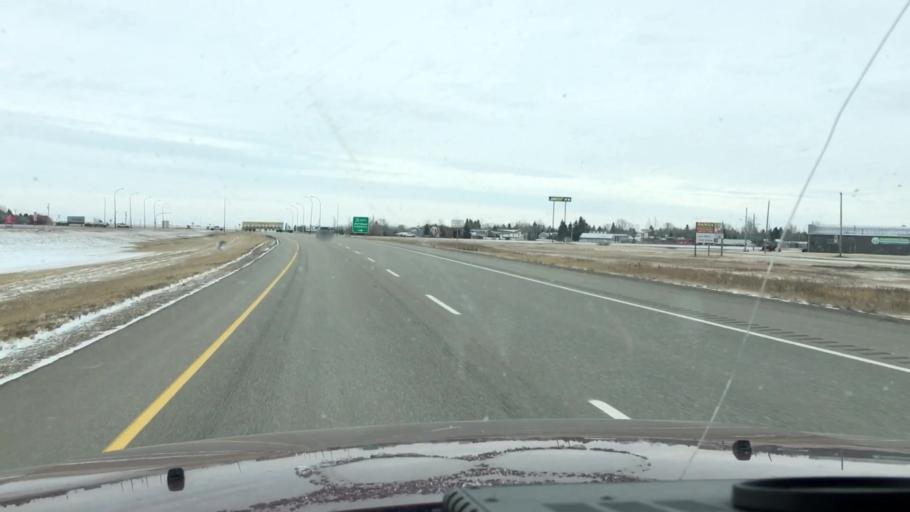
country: CA
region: Saskatchewan
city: Watrous
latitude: 51.2716
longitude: -105.9995
